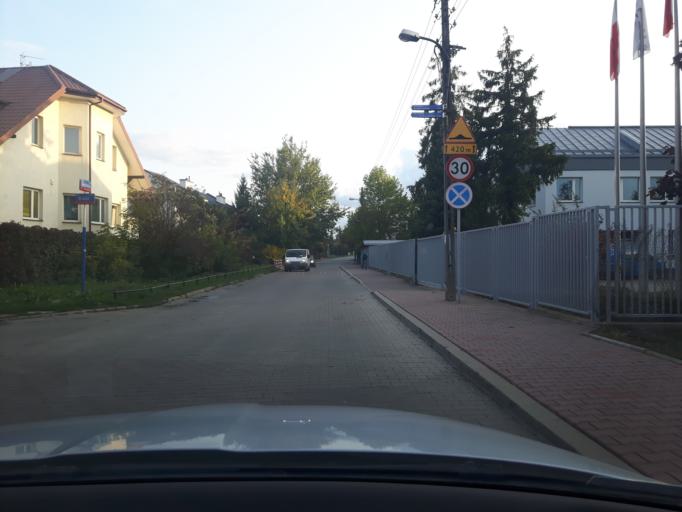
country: PL
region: Masovian Voivodeship
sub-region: Warszawa
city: Ursynow
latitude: 52.1512
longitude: 21.0225
